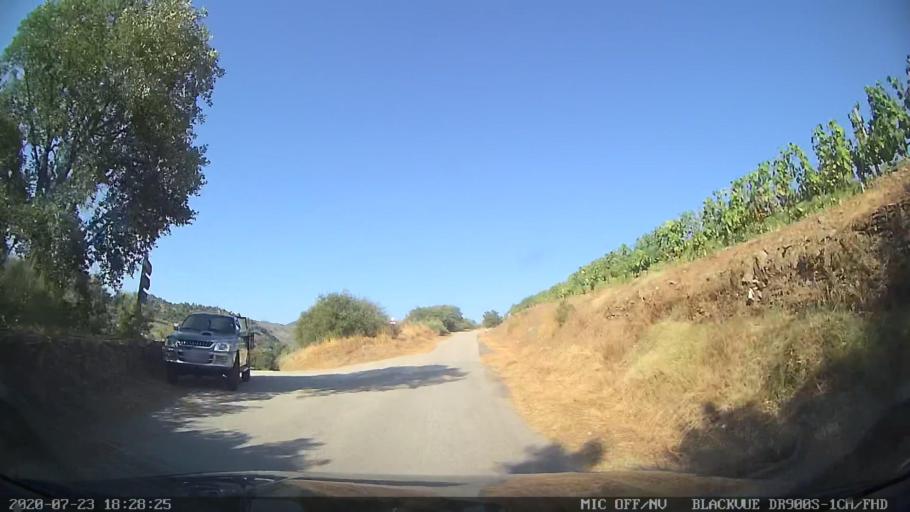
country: PT
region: Viseu
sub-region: Sao Joao da Pesqueira
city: Sao Joao da Pesqueira
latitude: 41.1860
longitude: -7.4029
